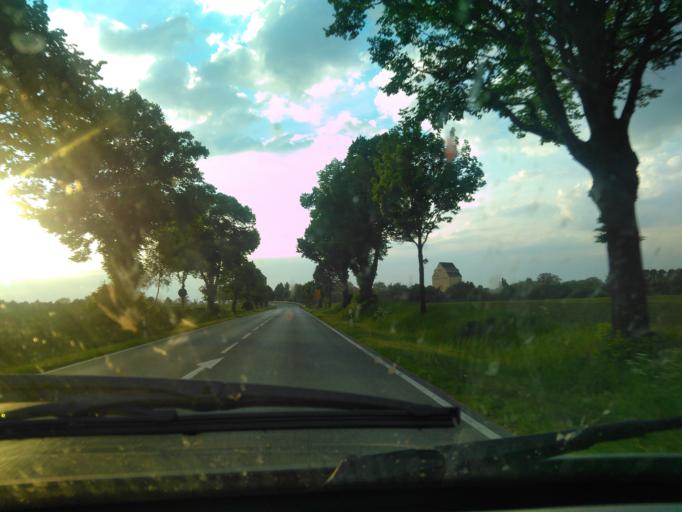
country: DE
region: Saxony-Anhalt
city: Stossen
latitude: 51.1074
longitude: 11.9325
